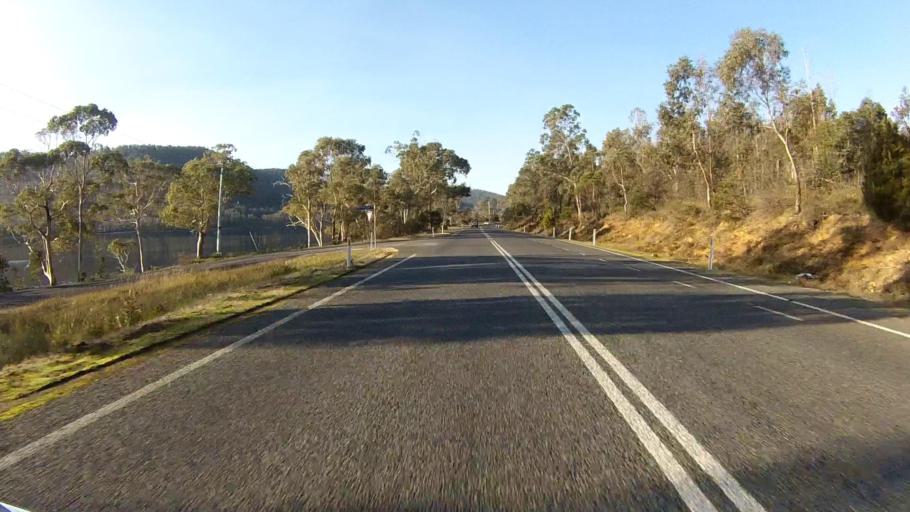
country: AU
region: Tasmania
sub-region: Clarence
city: Sandford
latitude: -43.0249
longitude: 147.8825
